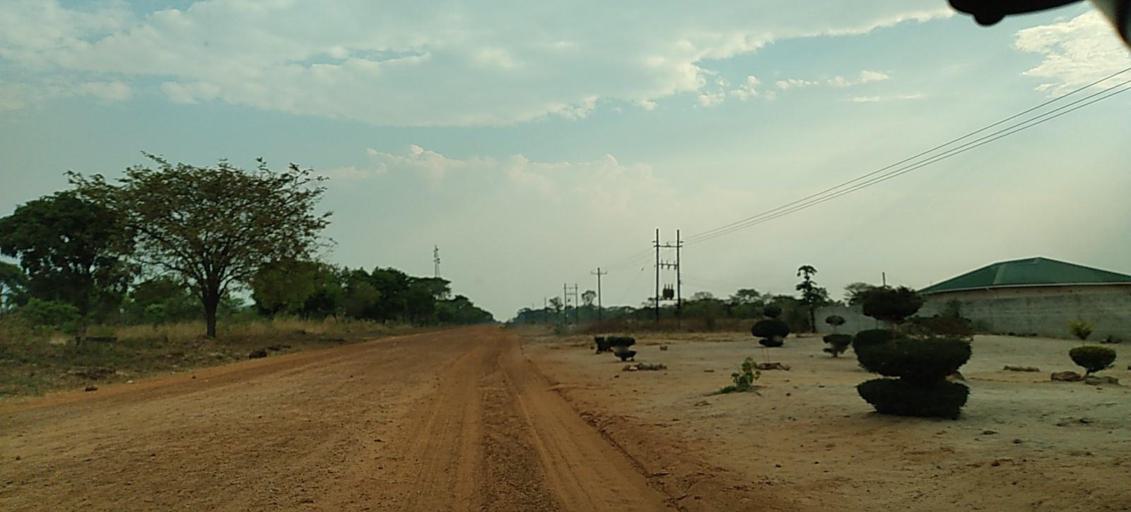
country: ZM
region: North-Western
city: Kabompo
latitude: -13.8795
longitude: 23.6644
